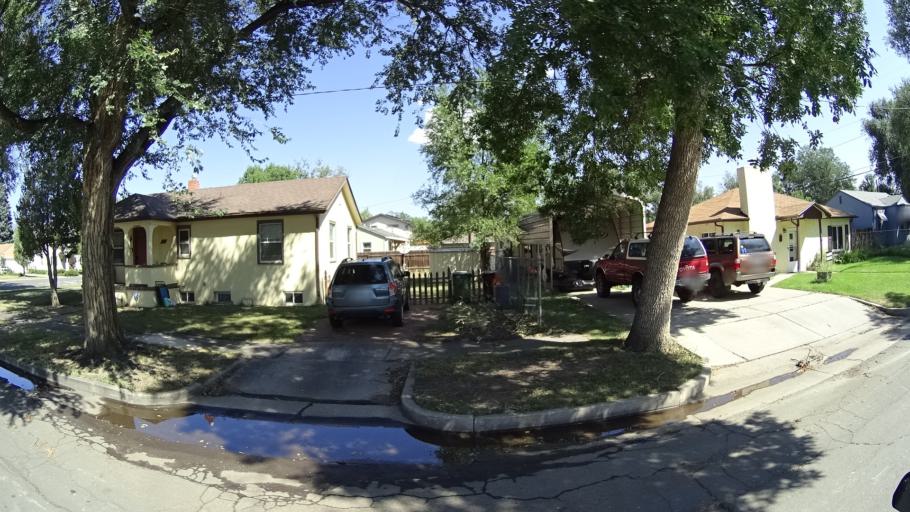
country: US
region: Colorado
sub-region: El Paso County
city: Colorado Springs
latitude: 38.8629
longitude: -104.8143
